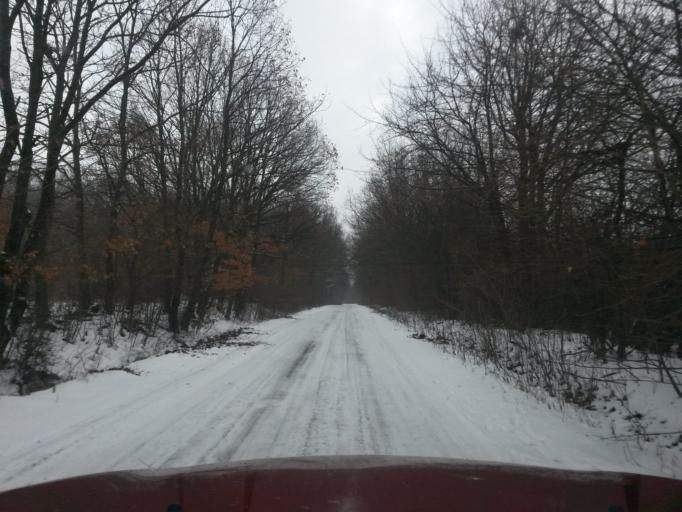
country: SK
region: Kosicky
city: Secovce
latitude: 48.8015
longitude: 21.4967
